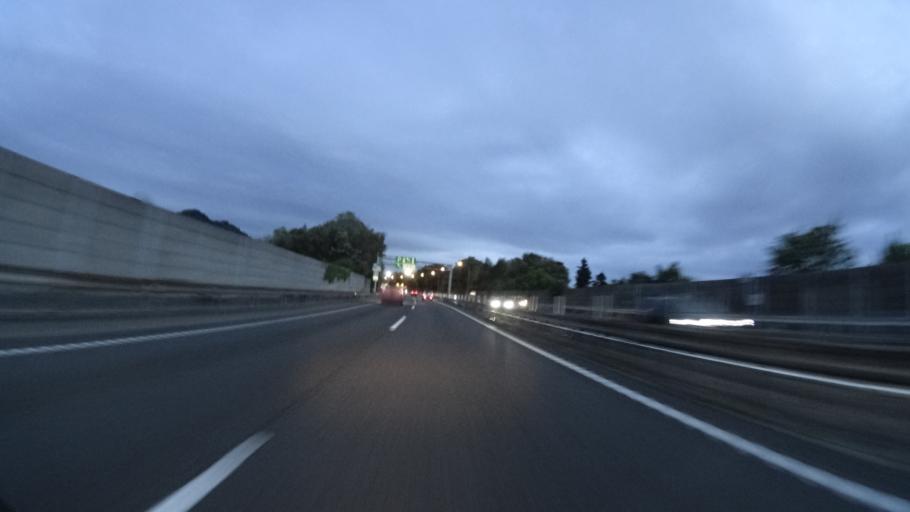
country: JP
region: Shiga Prefecture
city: Hikone
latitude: 35.2244
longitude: 136.2826
